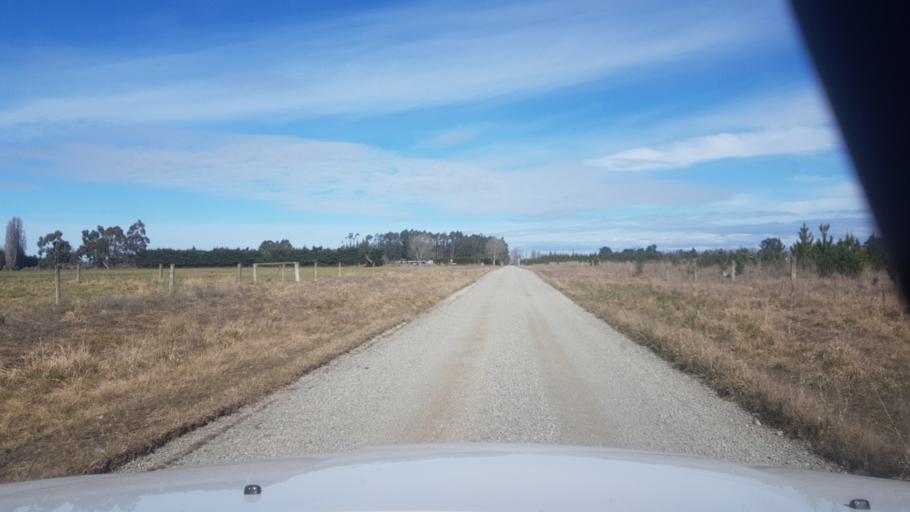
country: NZ
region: Canterbury
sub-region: Timaru District
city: Pleasant Point
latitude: -44.1335
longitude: 171.2789
